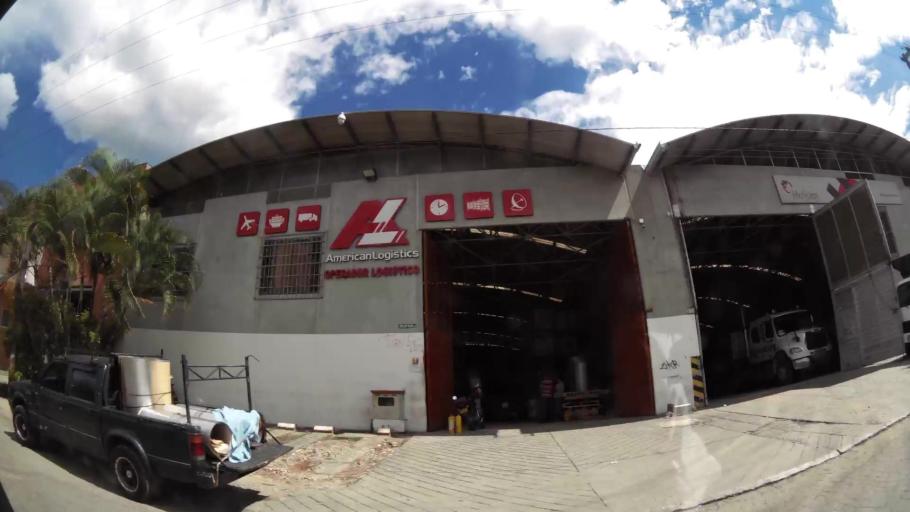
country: CO
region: Antioquia
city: Sabaneta
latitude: 6.1586
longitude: -75.6137
